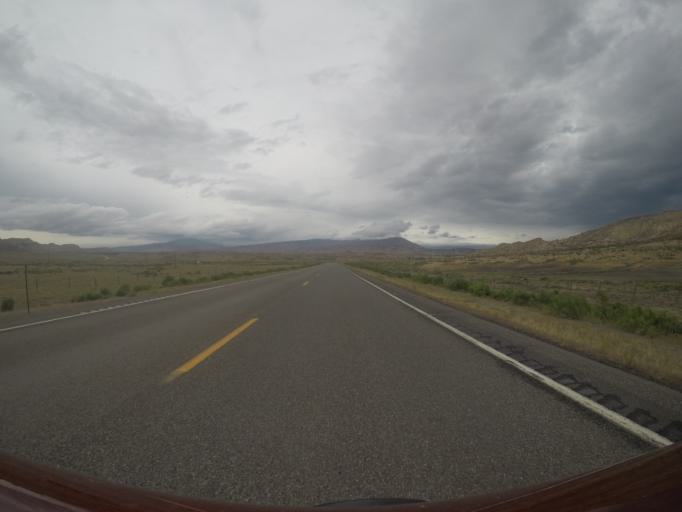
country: US
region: Wyoming
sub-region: Big Horn County
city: Lovell
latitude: 44.9443
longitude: -108.2967
